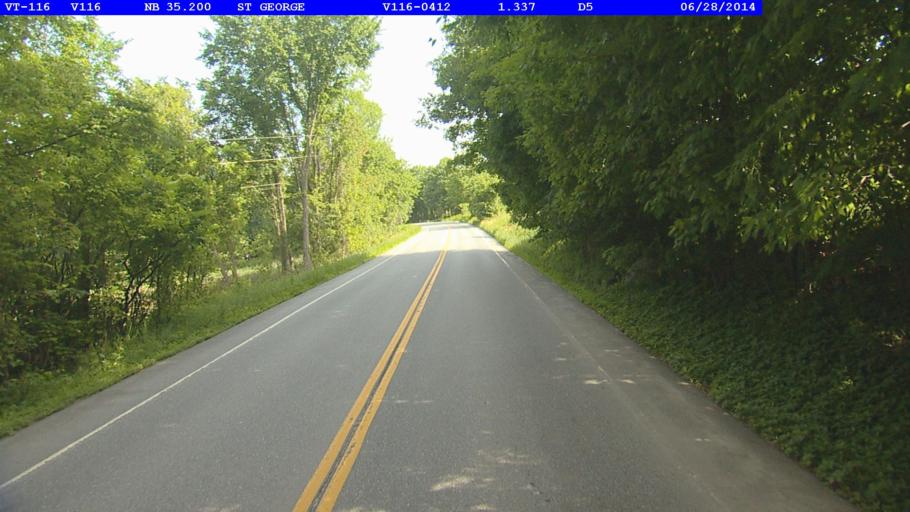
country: US
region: Vermont
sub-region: Chittenden County
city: Hinesburg
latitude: 44.3972
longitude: -73.1397
